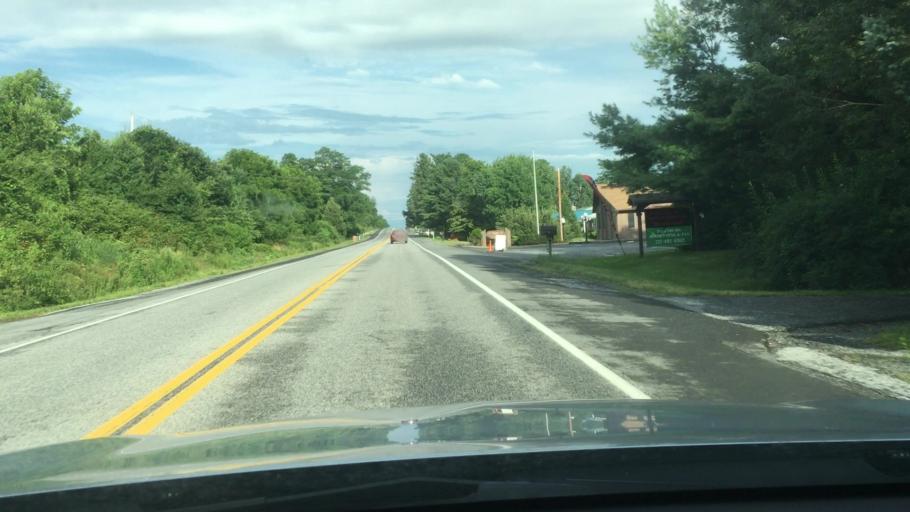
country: US
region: Pennsylvania
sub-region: York County
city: Dillsburg
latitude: 40.0987
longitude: -76.9762
